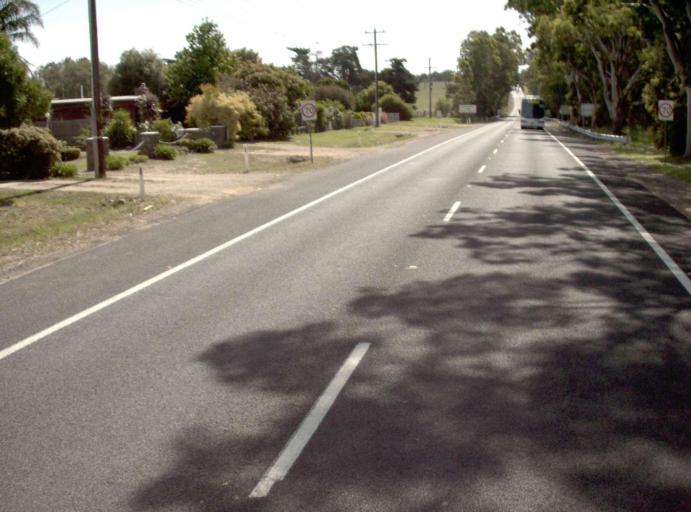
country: AU
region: Victoria
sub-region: East Gippsland
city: Lakes Entrance
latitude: -37.8198
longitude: 147.8283
